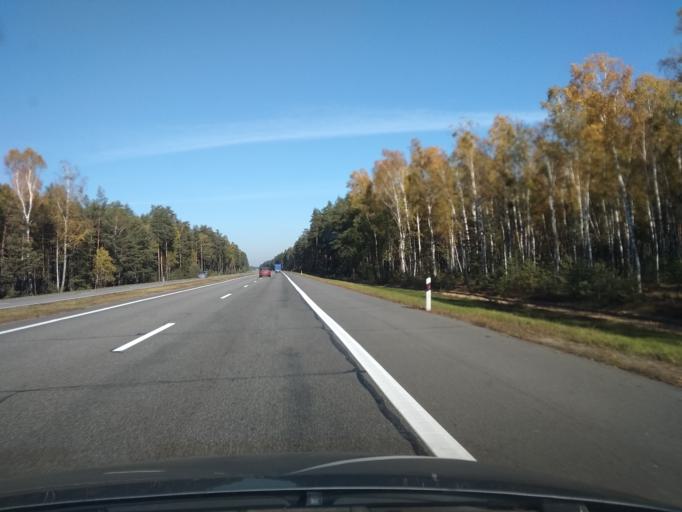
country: BY
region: Brest
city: Baranovichi
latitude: 52.9670
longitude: 25.7338
